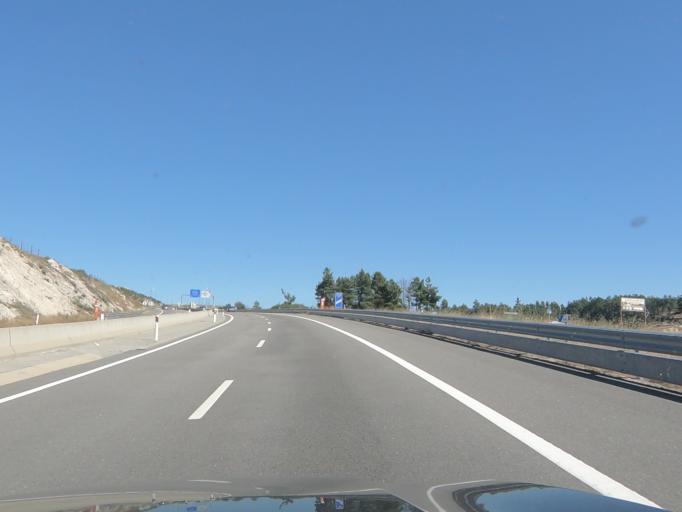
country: PT
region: Vila Real
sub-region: Murca
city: Murca
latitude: 41.3784
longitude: -7.5203
